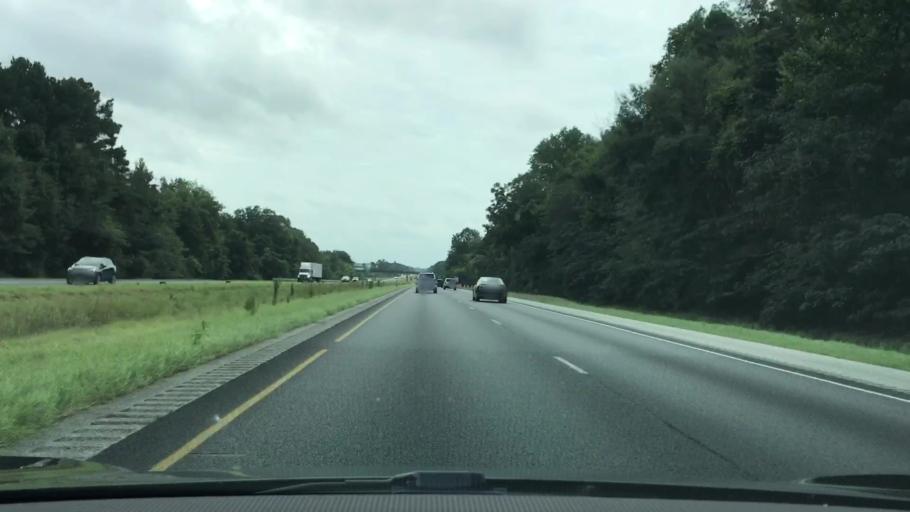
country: US
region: Alabama
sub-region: Montgomery County
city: Pike Road
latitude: 32.3711
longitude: -86.0442
